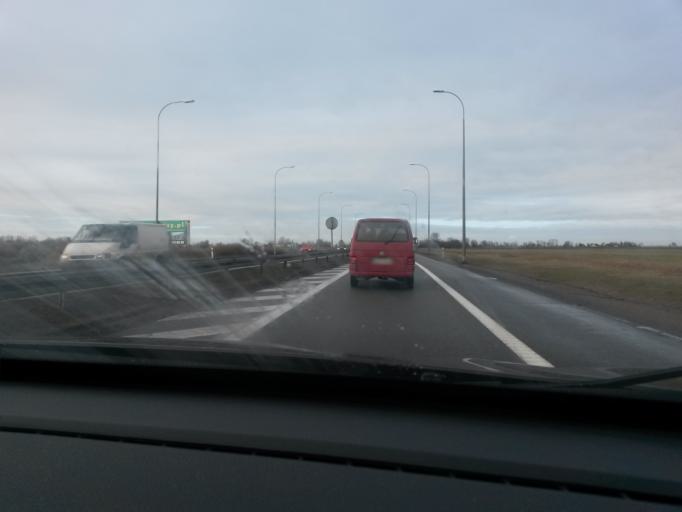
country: PL
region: Pomeranian Voivodeship
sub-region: Powiat nowodworski
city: Nowy Dwor Gdanski
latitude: 54.2176
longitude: 19.0886
